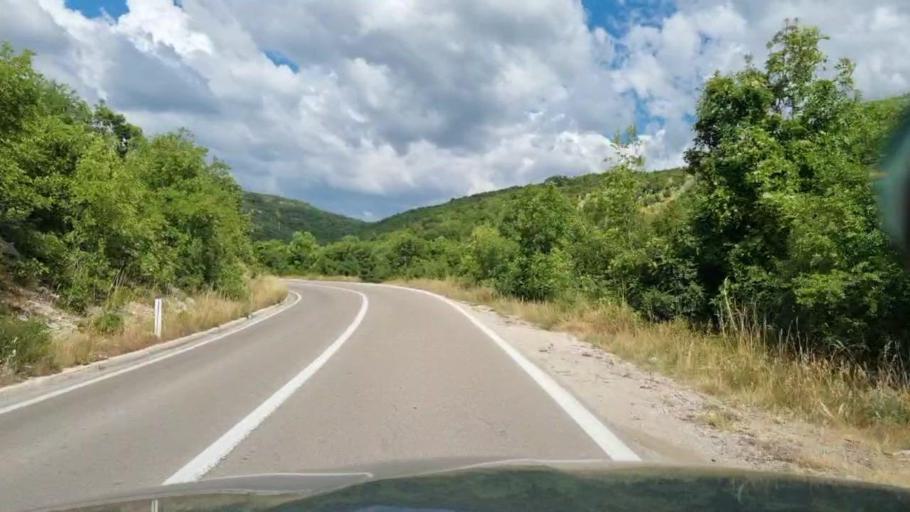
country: BA
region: Republika Srpska
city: Nevesinje
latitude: 43.2629
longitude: 18.0125
